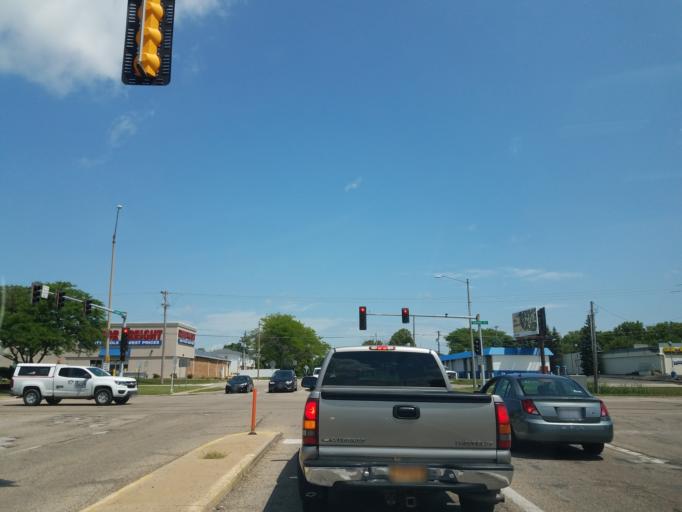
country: US
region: Illinois
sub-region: McLean County
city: Bloomington
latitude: 40.4881
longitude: -88.9611
